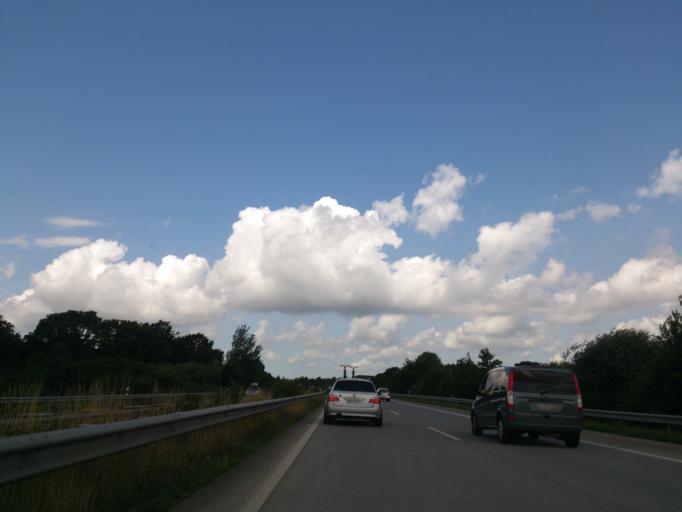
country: DE
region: Schleswig-Holstein
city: Dageling
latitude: 53.8826
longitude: 9.5460
